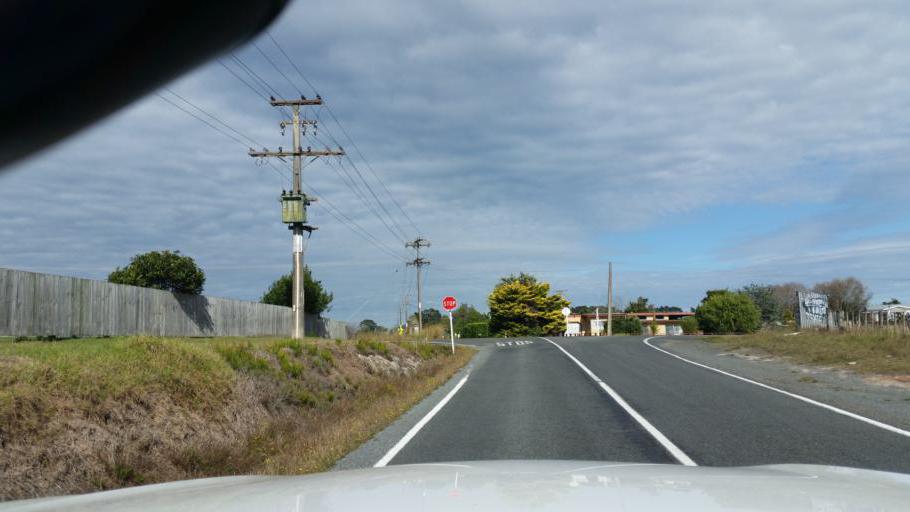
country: NZ
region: Northland
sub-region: Kaipara District
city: Dargaville
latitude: -35.9184
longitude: 173.8197
